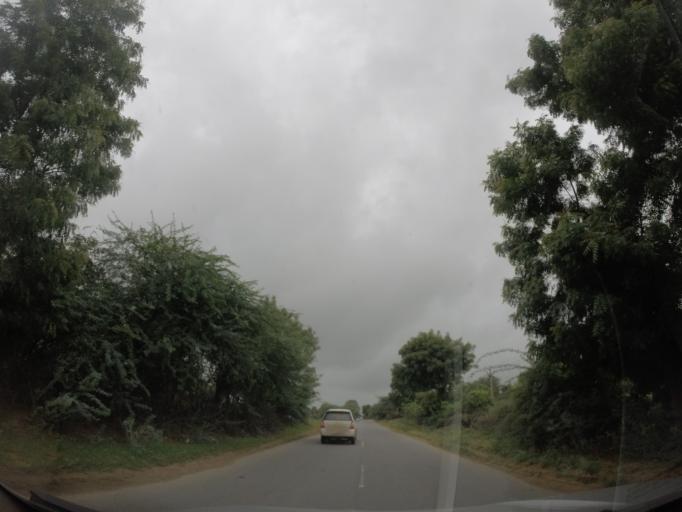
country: IN
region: Gujarat
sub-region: Banas Kantha
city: Dhanera
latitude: 24.6215
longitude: 71.9148
